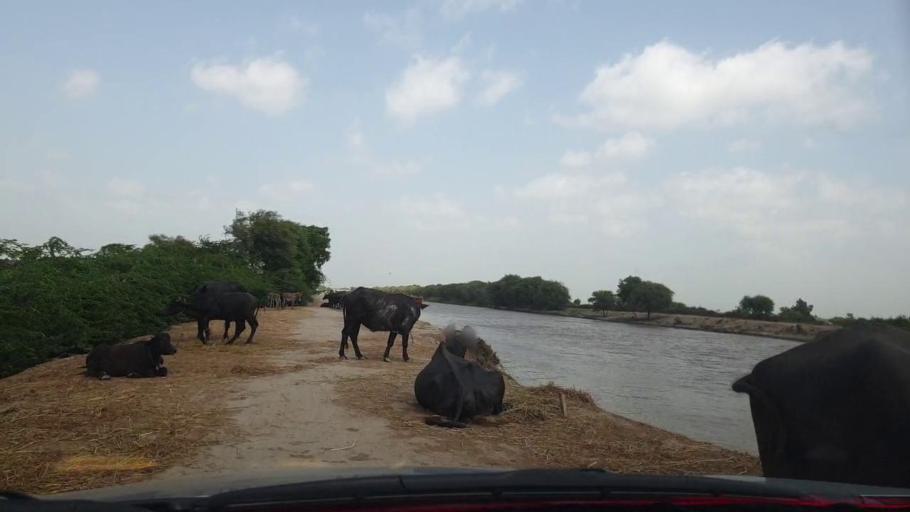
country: PK
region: Sindh
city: Talhar
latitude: 24.8959
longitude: 68.8358
